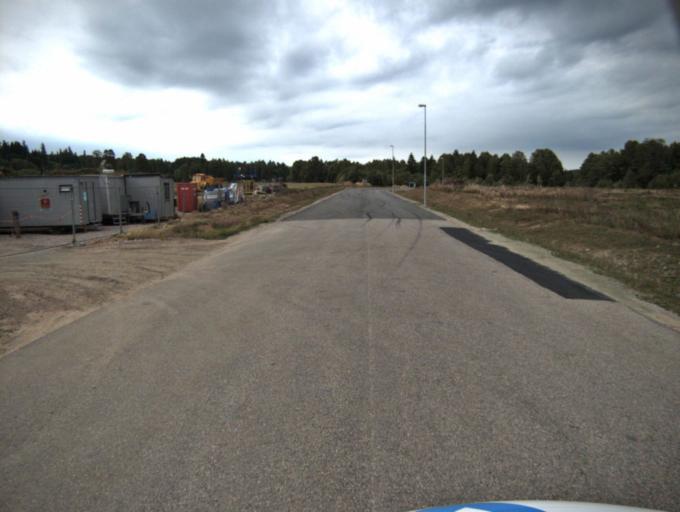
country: SE
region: Vaestra Goetaland
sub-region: Ulricehamns Kommun
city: Ulricehamn
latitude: 57.8401
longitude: 13.4238
